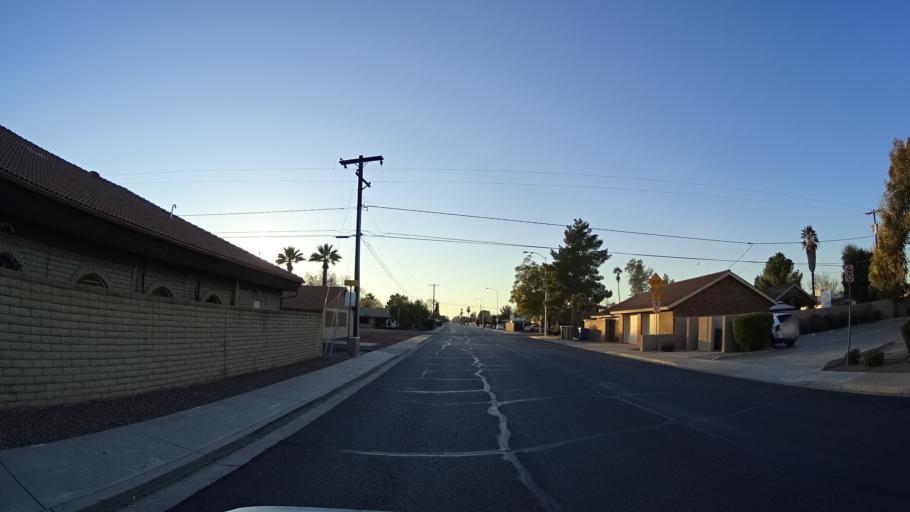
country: US
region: Arizona
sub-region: Maricopa County
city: Mesa
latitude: 33.4260
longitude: -111.8056
